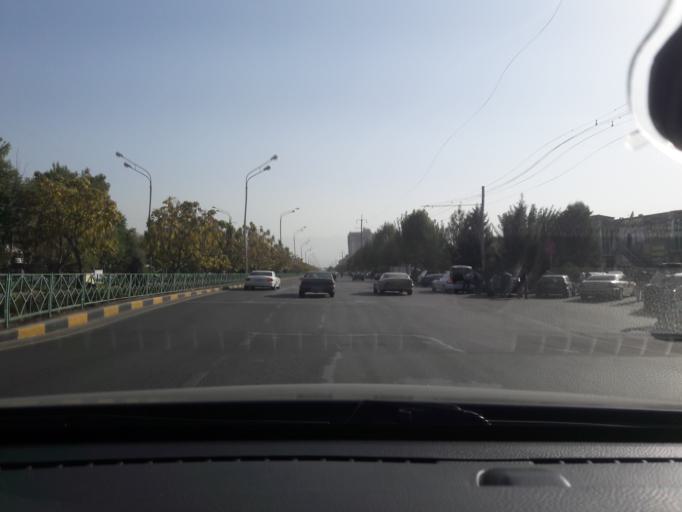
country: TJ
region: Dushanbe
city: Dushanbe
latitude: 38.5234
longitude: 68.7618
